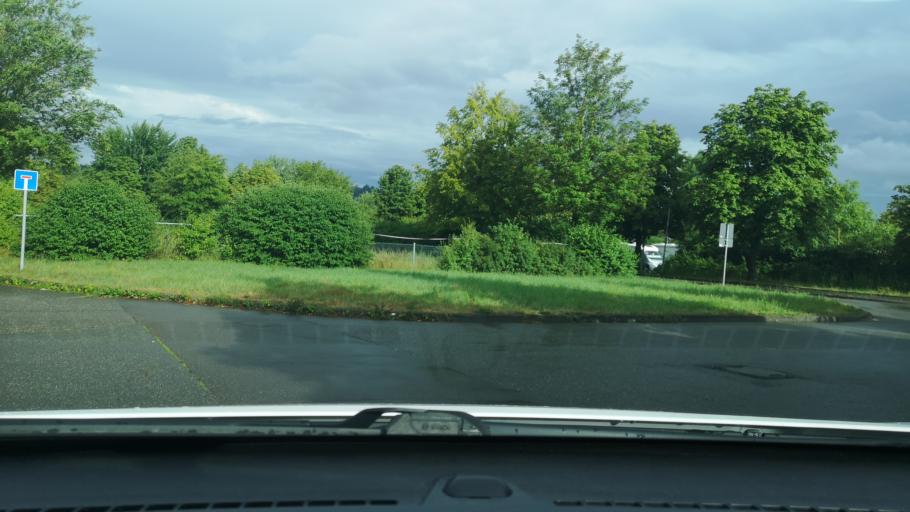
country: DE
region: Baden-Wuerttemberg
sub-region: Freiburg Region
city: Rottweil
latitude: 48.1558
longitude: 8.6281
